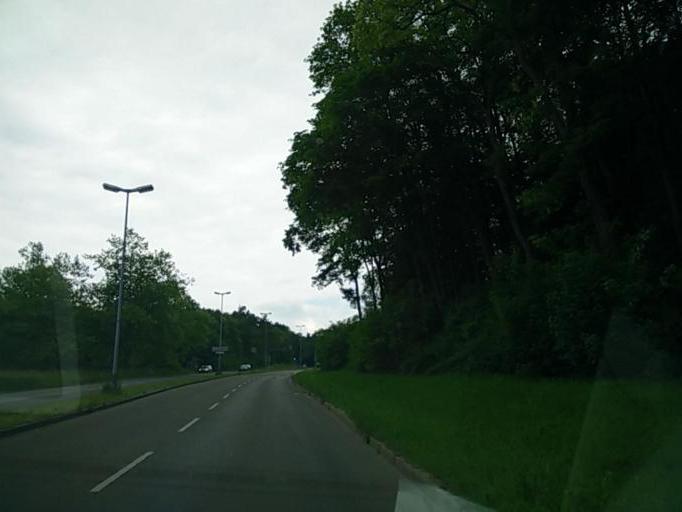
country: DE
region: Baden-Wuerttemberg
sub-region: Tuebingen Region
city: Tuebingen
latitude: 48.5369
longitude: 9.0679
